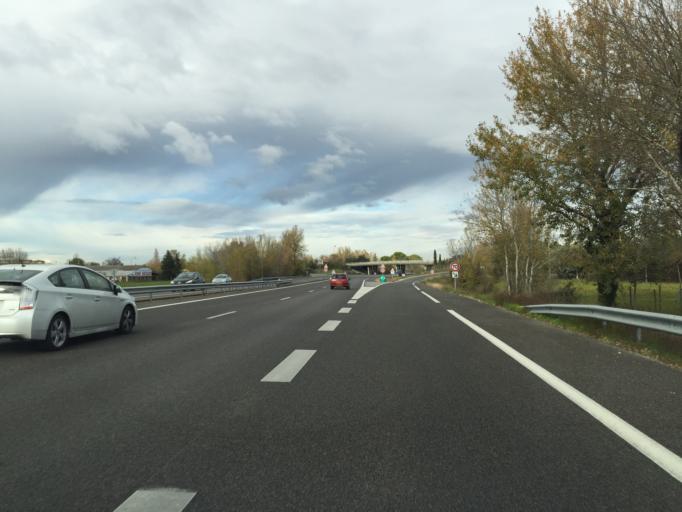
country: FR
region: Provence-Alpes-Cote d'Azur
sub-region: Departement du Vaucluse
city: Althen-des-Paluds
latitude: 44.0047
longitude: 4.9416
